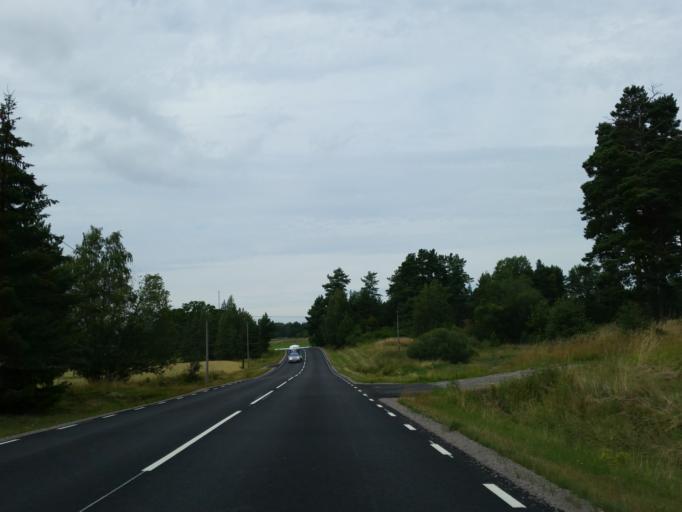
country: SE
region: Soedermanland
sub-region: Strangnas Kommun
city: Akers Styckebruk
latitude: 59.2719
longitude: 17.1472
